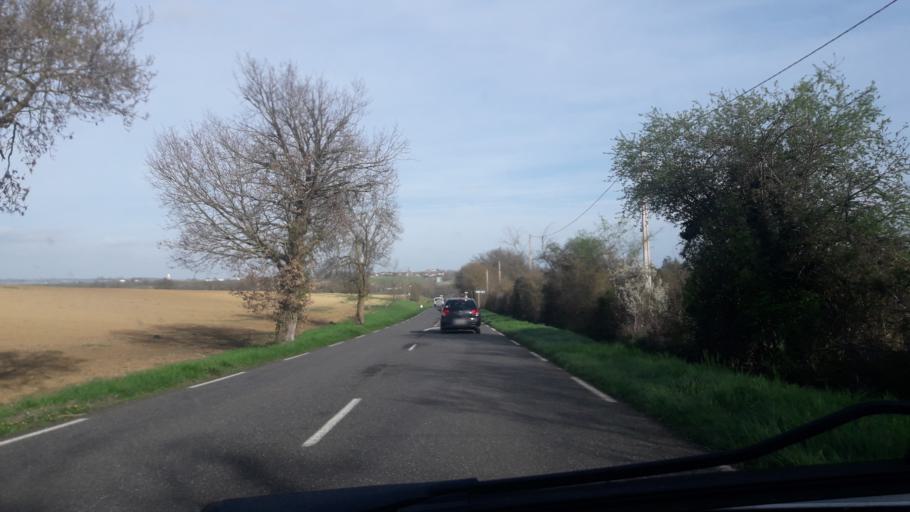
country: FR
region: Midi-Pyrenees
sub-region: Departement du Gers
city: Gimont
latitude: 43.7203
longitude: 0.9474
